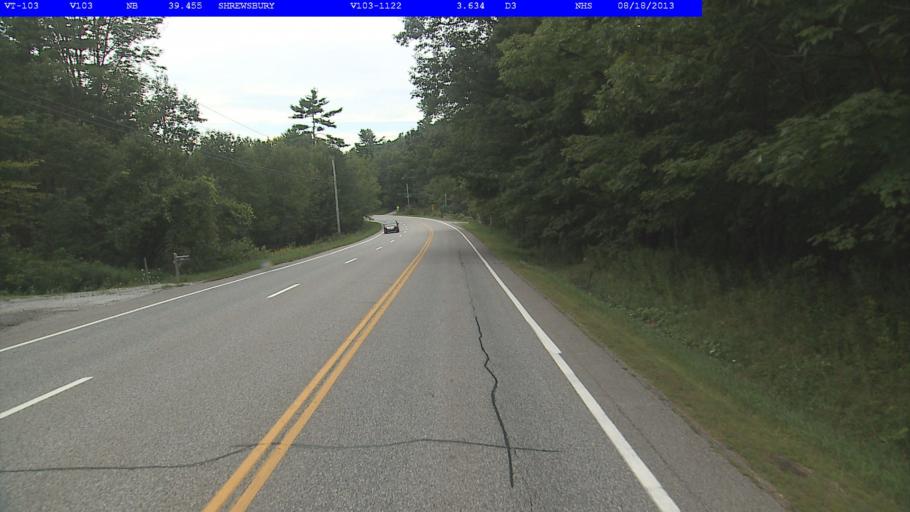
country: US
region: Vermont
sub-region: Rutland County
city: Rutland
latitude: 43.5190
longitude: -72.9215
